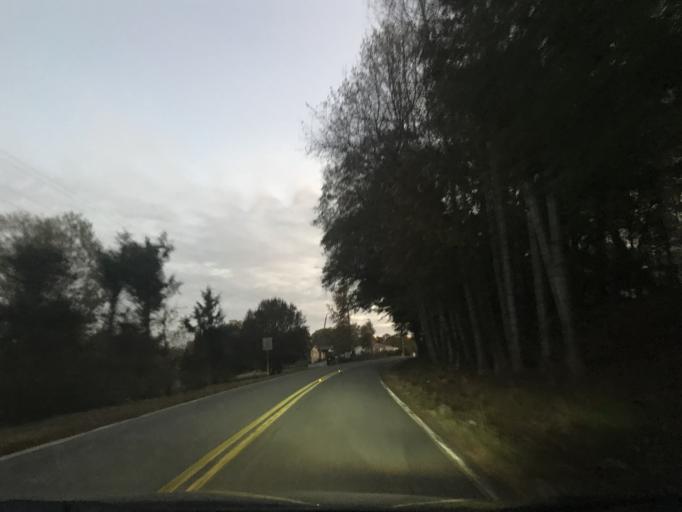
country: US
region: South Carolina
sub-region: Spartanburg County
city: Mayo
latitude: 35.0813
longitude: -81.9001
